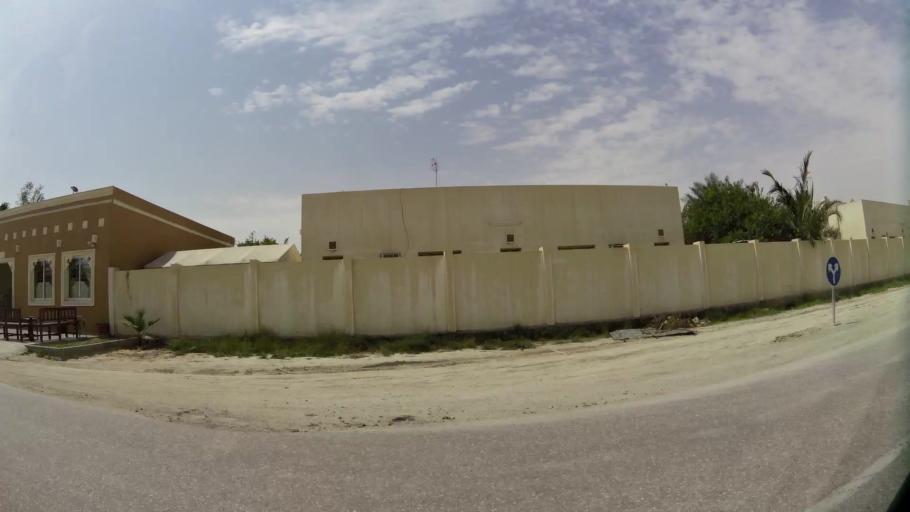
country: QA
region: Baladiyat ar Rayyan
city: Ar Rayyan
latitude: 25.3521
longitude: 51.4764
